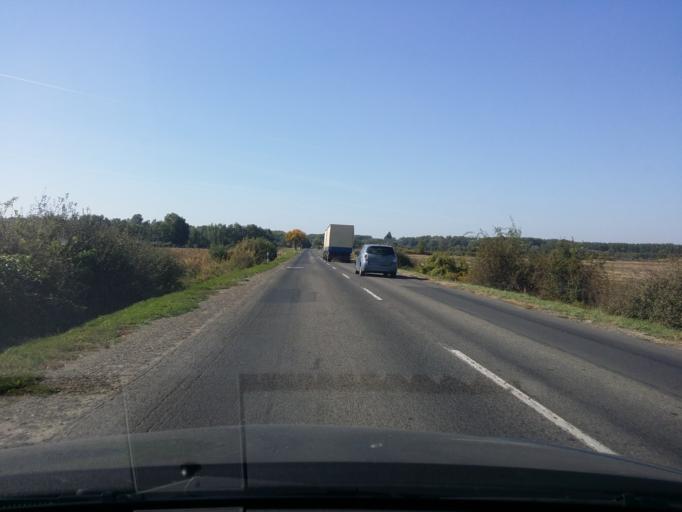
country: HU
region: Bacs-Kiskun
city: Tiszakecske
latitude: 46.8671
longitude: 20.0722
